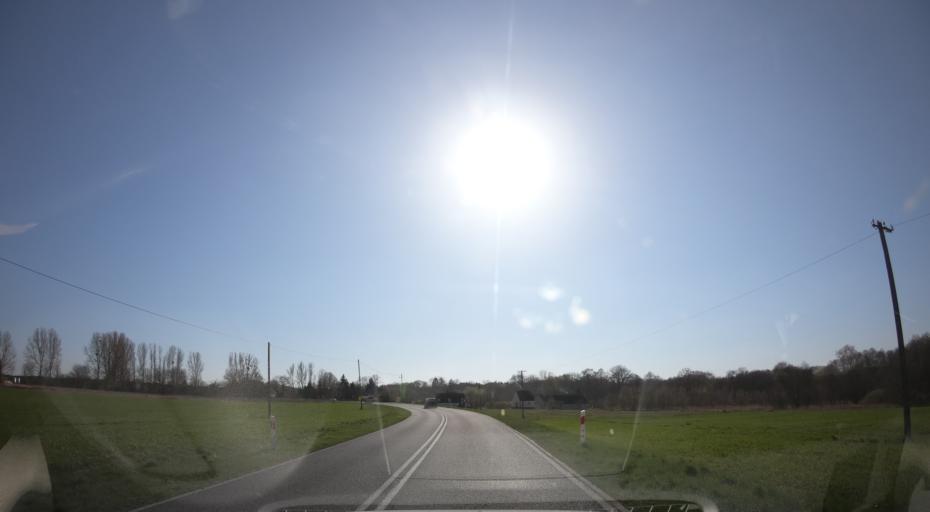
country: PL
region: West Pomeranian Voivodeship
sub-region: Powiat goleniowski
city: Przybiernow
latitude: 53.8618
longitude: 14.7631
